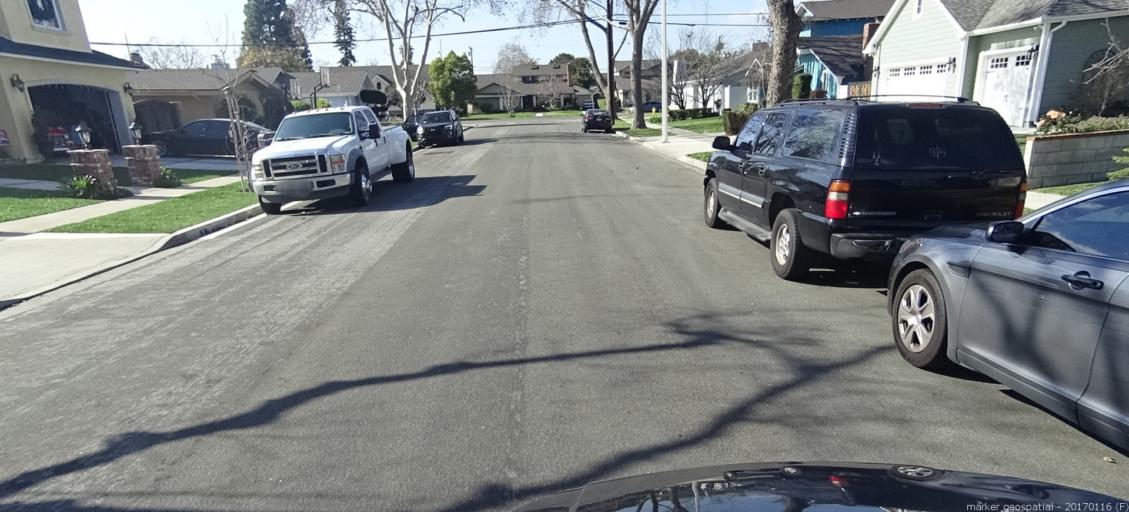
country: US
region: California
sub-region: Orange County
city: Rossmoor
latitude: 33.7789
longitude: -118.0775
